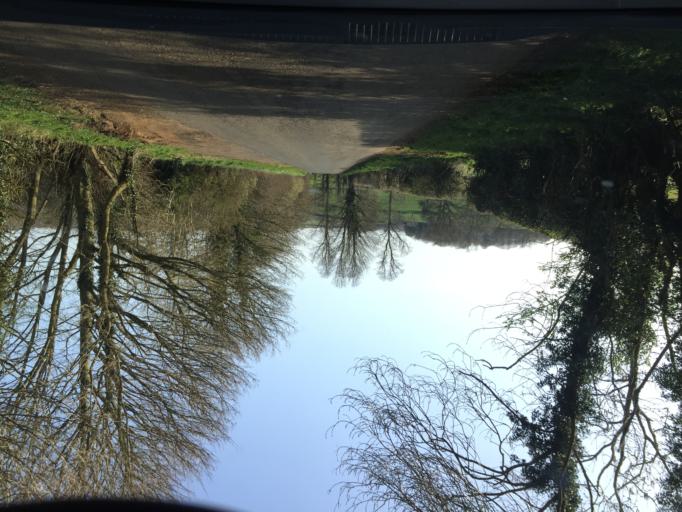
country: GB
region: England
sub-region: Oxfordshire
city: Bloxham
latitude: 52.0351
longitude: -1.3913
